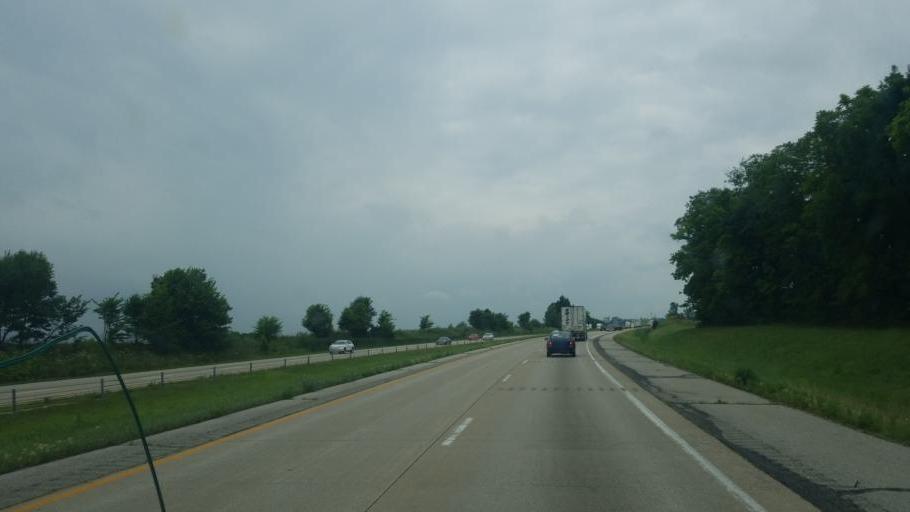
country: US
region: Indiana
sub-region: Grant County
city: Upland
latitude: 40.4606
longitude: -85.5512
